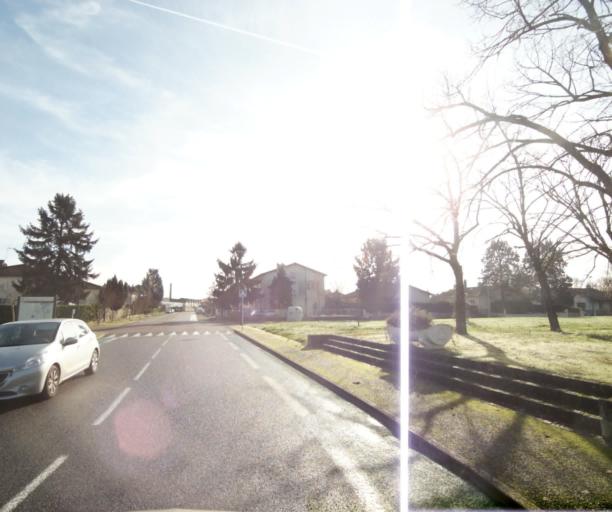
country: FR
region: Midi-Pyrenees
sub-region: Departement de la Haute-Garonne
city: Villemur-sur-Tarn
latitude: 43.8633
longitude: 1.4953
